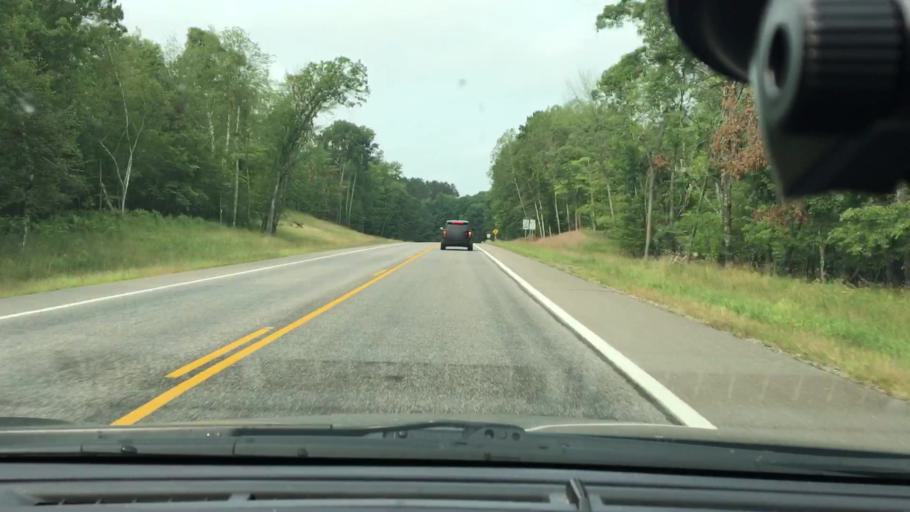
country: US
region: Minnesota
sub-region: Crow Wing County
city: Cross Lake
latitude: 46.6603
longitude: -94.0941
